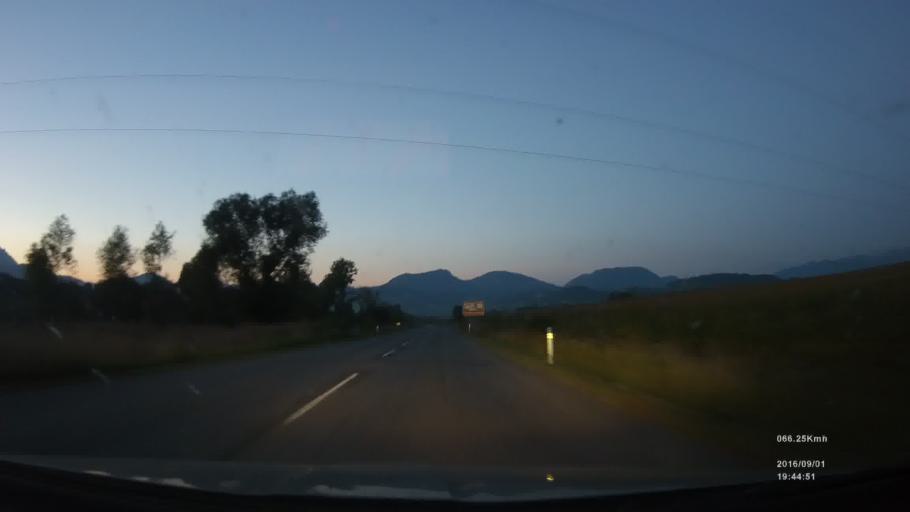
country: SK
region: Zilinsky
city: Ruzomberok
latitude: 49.0700
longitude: 19.4374
